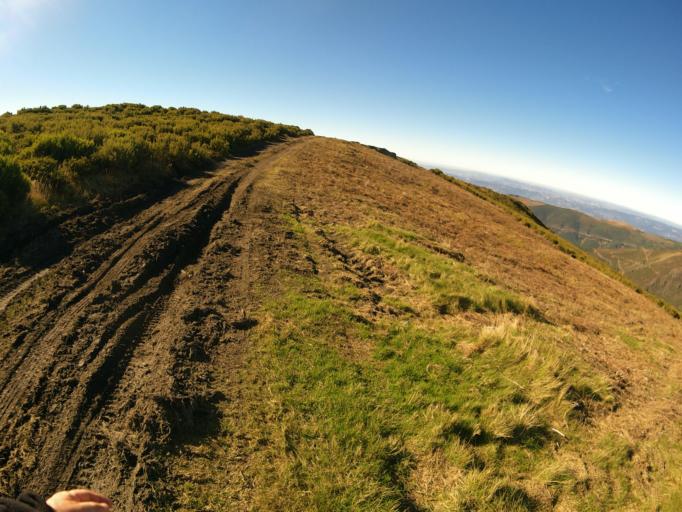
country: PT
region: Vila Real
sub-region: Mesao Frio
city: Mesao Frio
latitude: 41.2543
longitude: -7.9045
